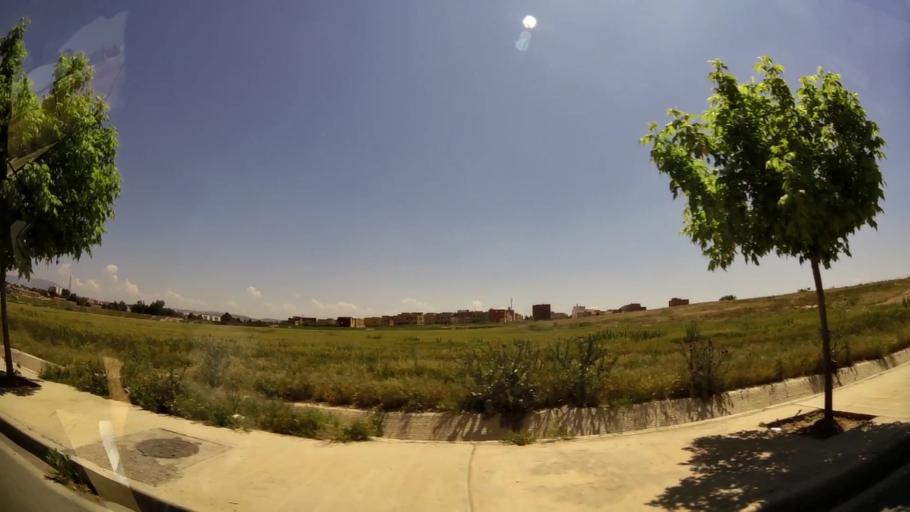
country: MA
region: Oriental
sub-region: Oujda-Angad
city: Oujda
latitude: 34.6945
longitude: -1.9272
